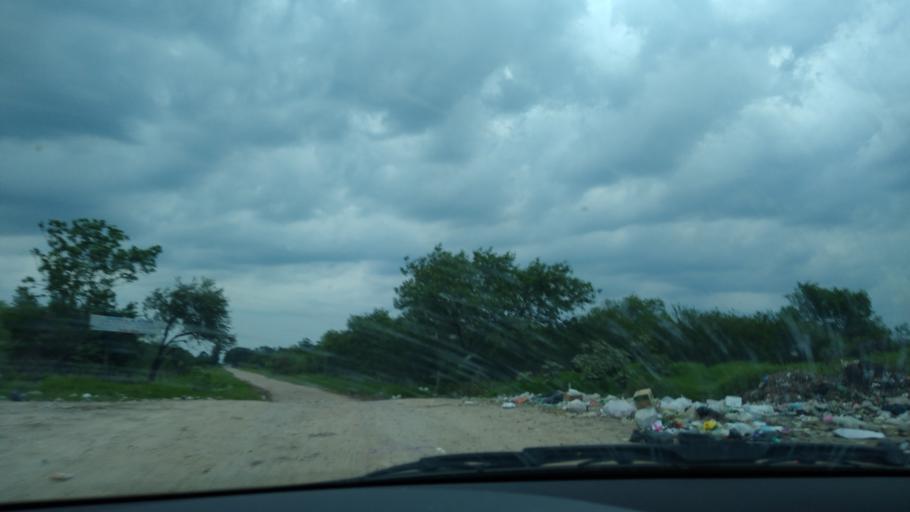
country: AR
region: Chaco
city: Puerto Vilelas
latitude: -27.5091
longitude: -58.9655
